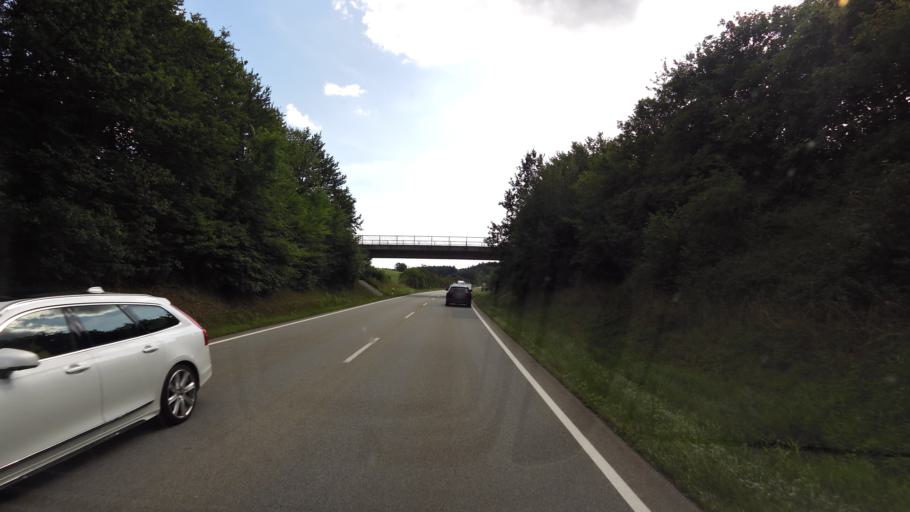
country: DE
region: Bavaria
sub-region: Lower Bavaria
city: Rattiszell
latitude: 49.0277
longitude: 12.6528
